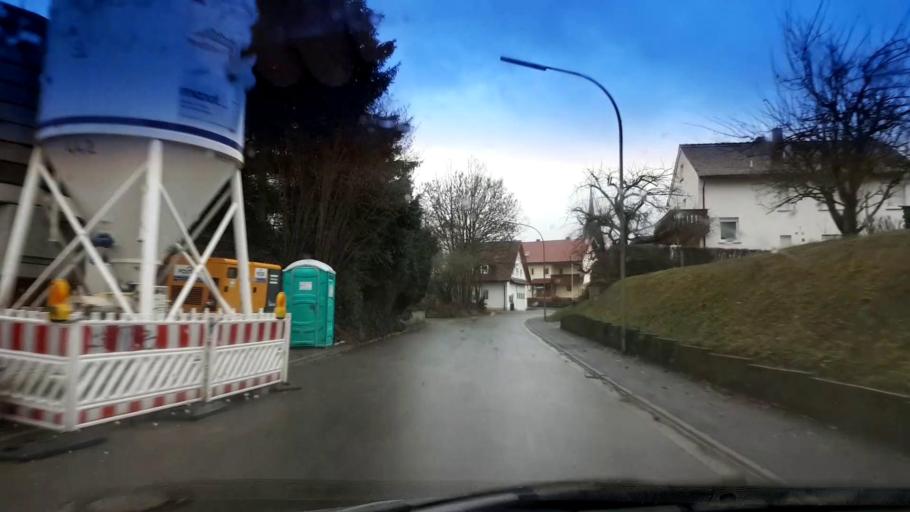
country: DE
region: Bavaria
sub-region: Upper Franconia
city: Litzendorf
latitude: 49.8735
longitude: 11.0447
